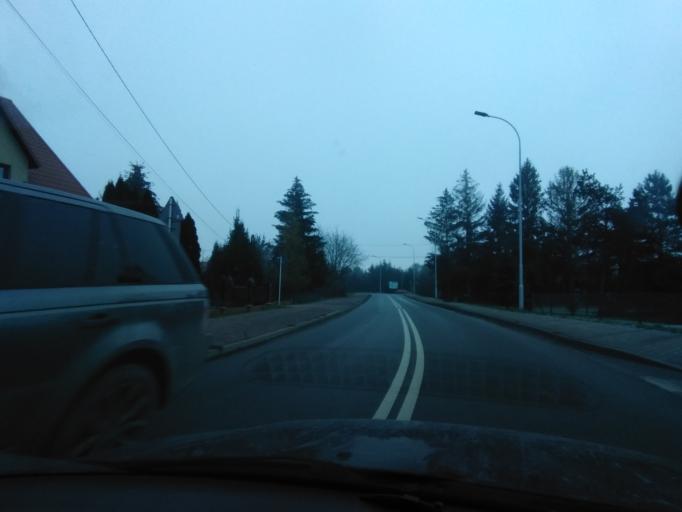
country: PL
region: Subcarpathian Voivodeship
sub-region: Powiat rzeszowski
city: Boguchwala
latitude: 49.9923
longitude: 21.9841
